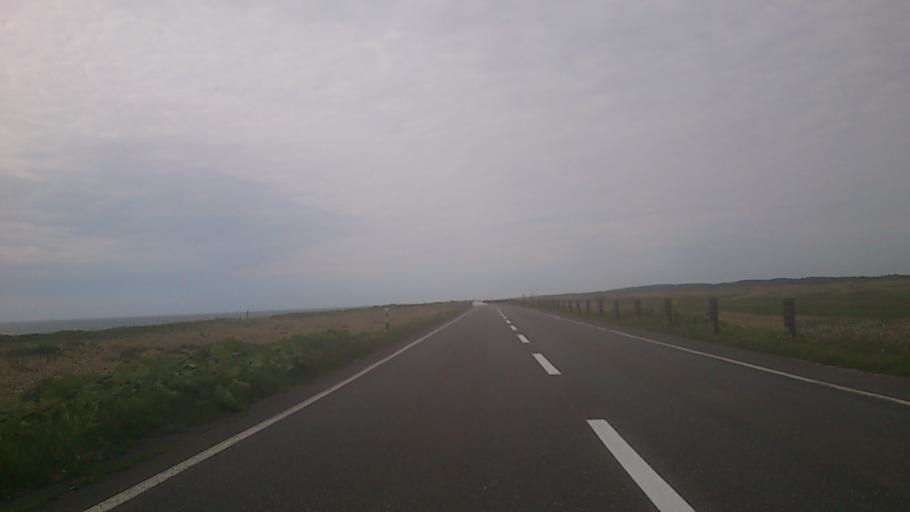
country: JP
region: Hokkaido
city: Wakkanai
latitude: 45.0459
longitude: 141.6558
